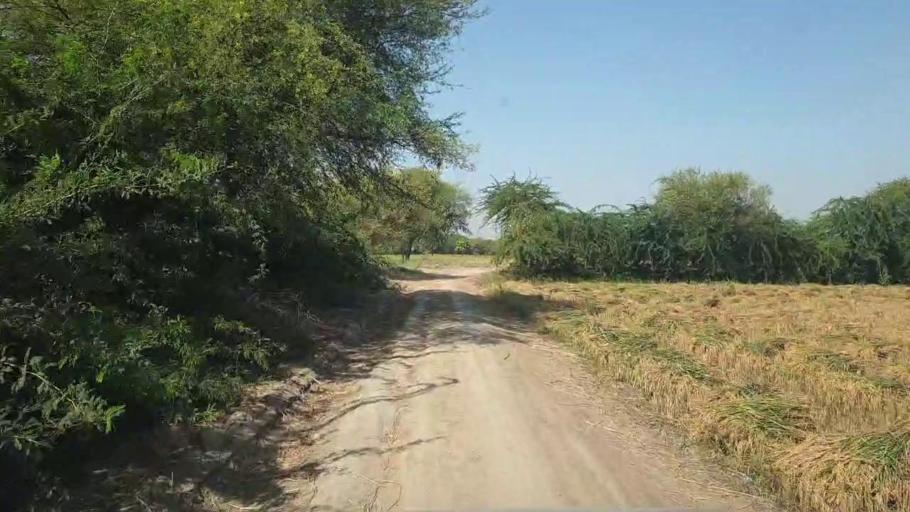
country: PK
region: Sindh
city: Talhar
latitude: 24.8131
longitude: 68.7845
